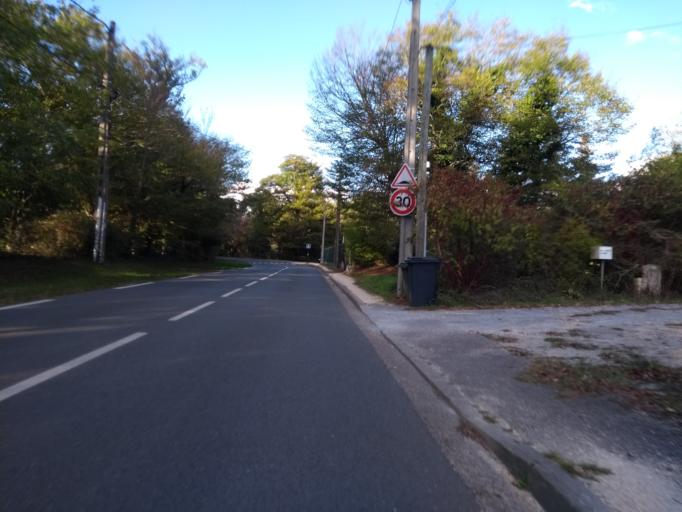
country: FR
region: Aquitaine
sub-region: Departement de la Gironde
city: Gradignan
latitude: 44.7607
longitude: -0.6145
